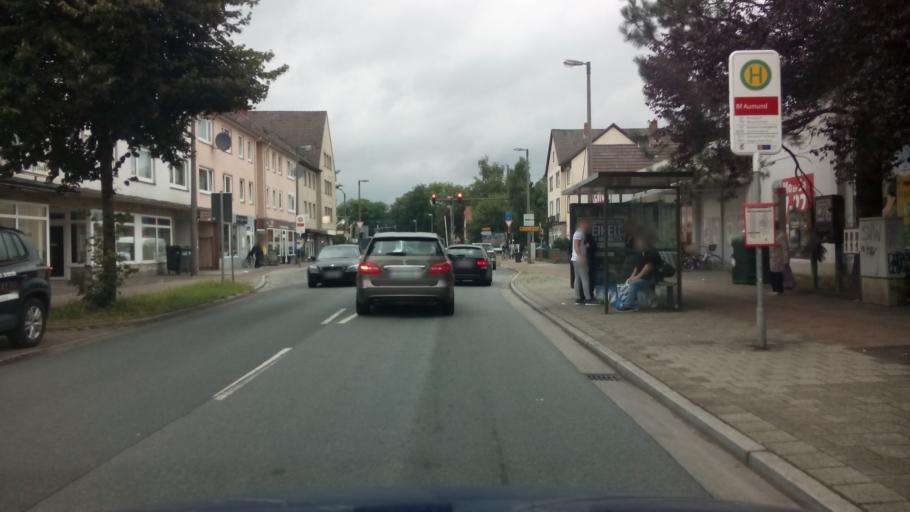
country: DE
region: Lower Saxony
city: Lemwerder
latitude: 53.1832
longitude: 8.6194
